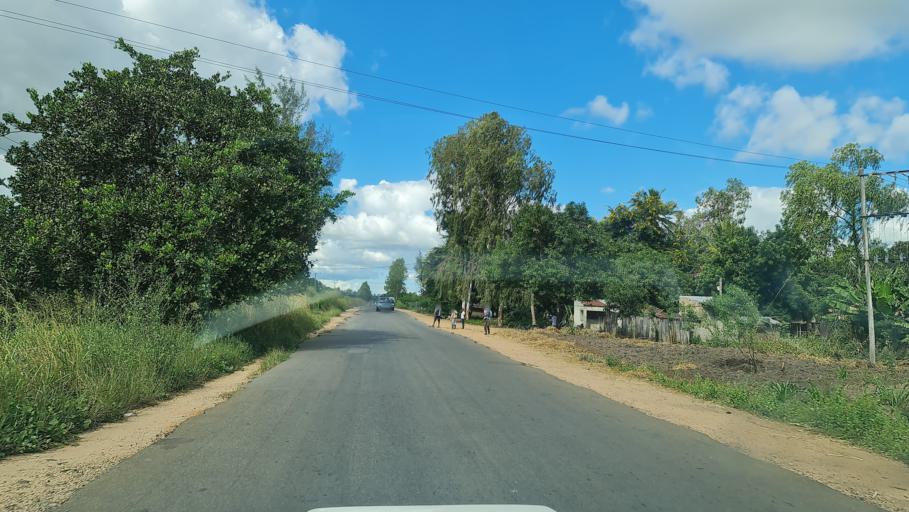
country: MZ
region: Zambezia
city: Quelimane
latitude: -17.5975
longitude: 36.7898
